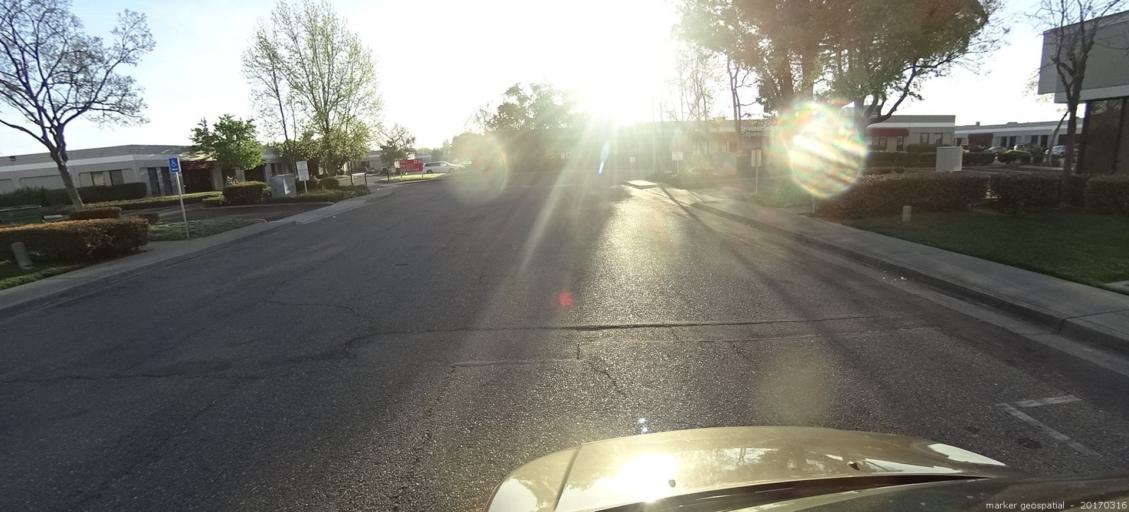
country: US
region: California
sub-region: Sacramento County
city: Parkway
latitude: 38.4996
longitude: -121.4650
